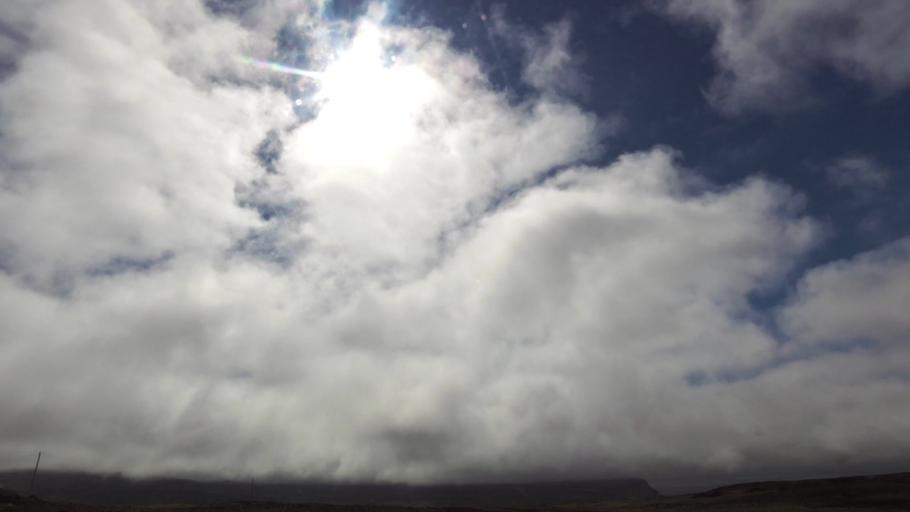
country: IS
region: West
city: Olafsvik
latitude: 65.5514
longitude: -24.2677
